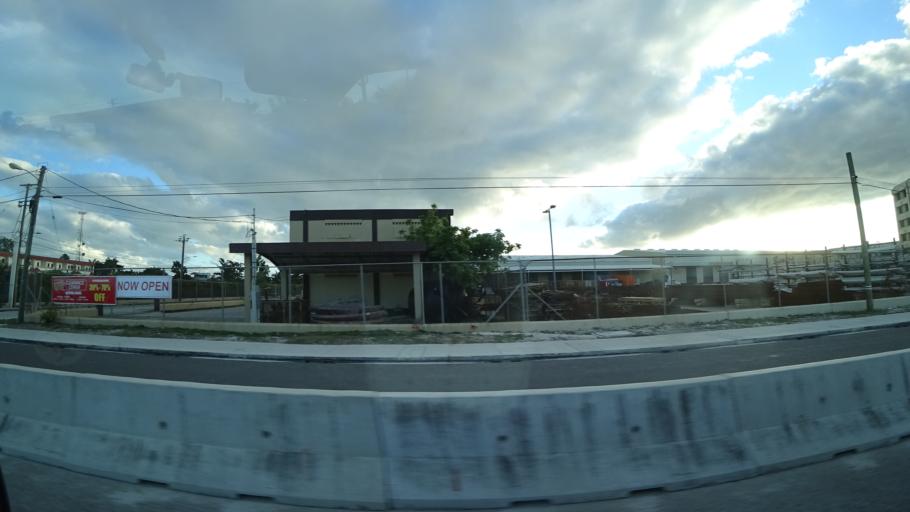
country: BZ
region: Belize
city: Belize City
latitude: 17.5125
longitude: -88.2182
